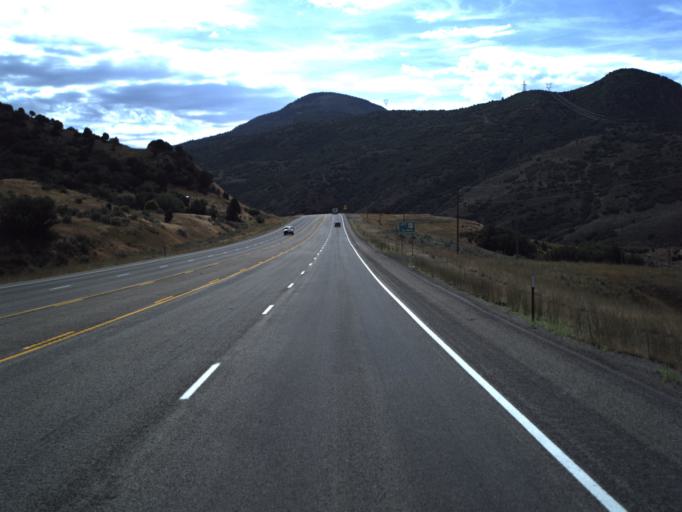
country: US
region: Utah
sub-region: Utah County
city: Mapleton
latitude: 39.9987
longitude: -111.4785
